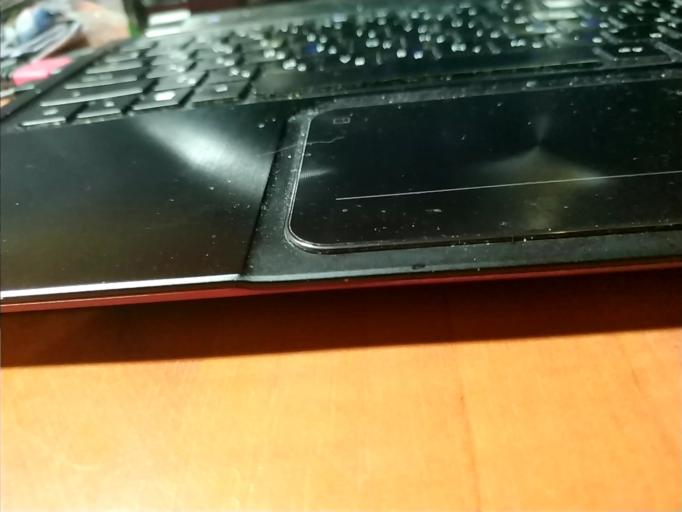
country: RU
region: Tverskaya
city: Ves'yegonsk
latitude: 58.6987
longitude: 37.5439
